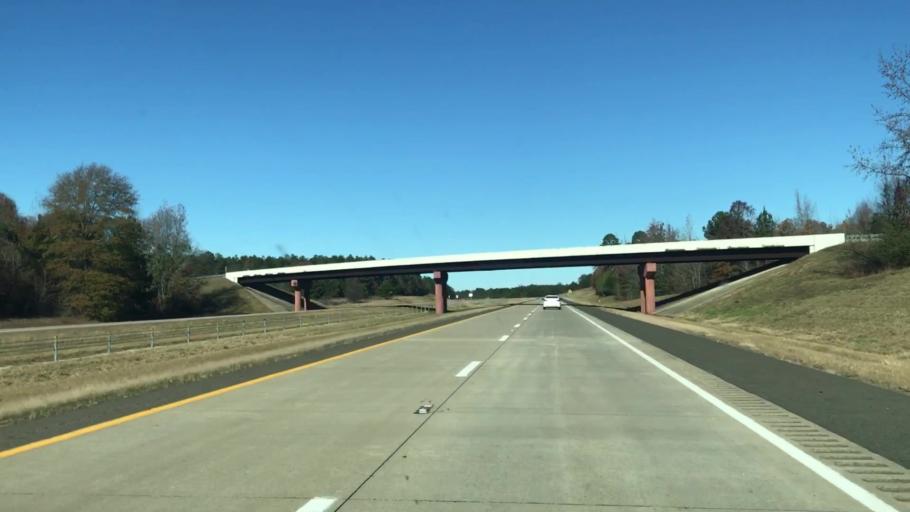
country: US
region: Texas
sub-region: Bowie County
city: Texarkana
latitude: 33.3308
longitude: -93.9591
